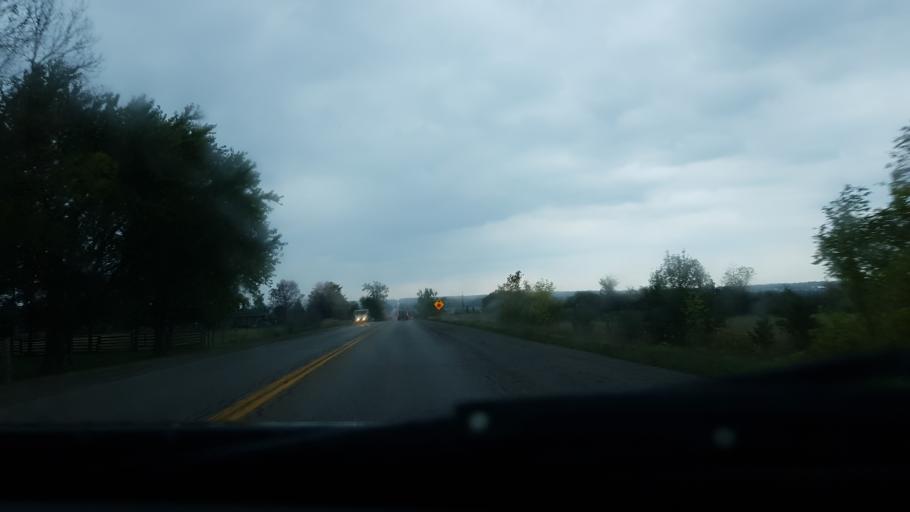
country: CA
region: Ontario
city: Omemee
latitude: 44.3833
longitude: -78.6042
